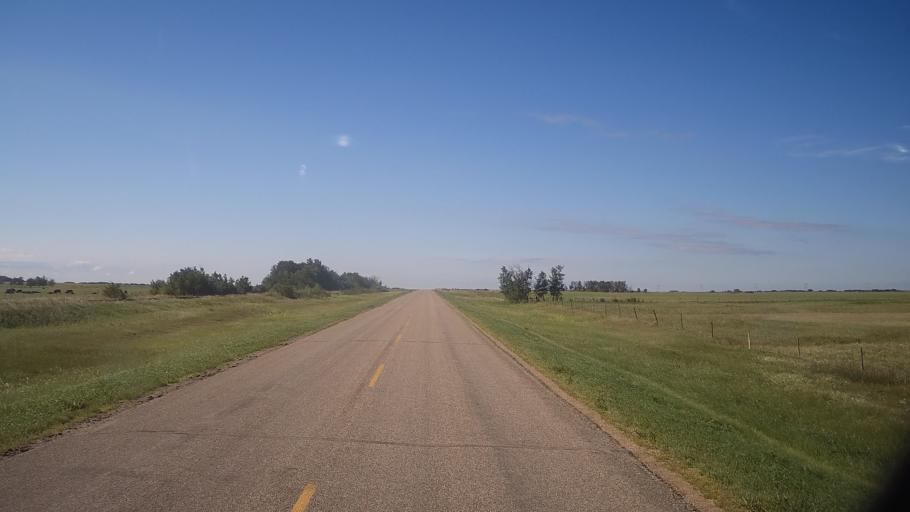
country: CA
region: Saskatchewan
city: Watrous
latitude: 51.7523
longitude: -105.2867
